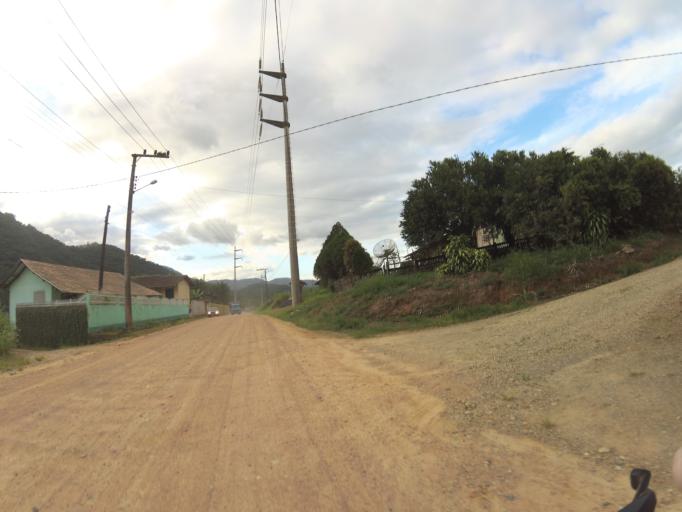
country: BR
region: Santa Catarina
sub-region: Pomerode
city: Pomerode
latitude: -26.7897
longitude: -49.1616
